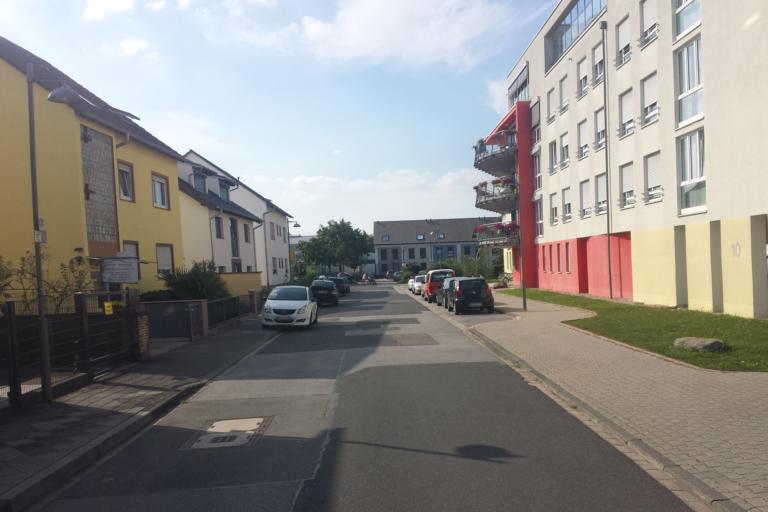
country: DE
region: Baden-Wuerttemberg
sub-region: Karlsruhe Region
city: Mannheim
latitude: 49.5227
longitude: 8.4925
